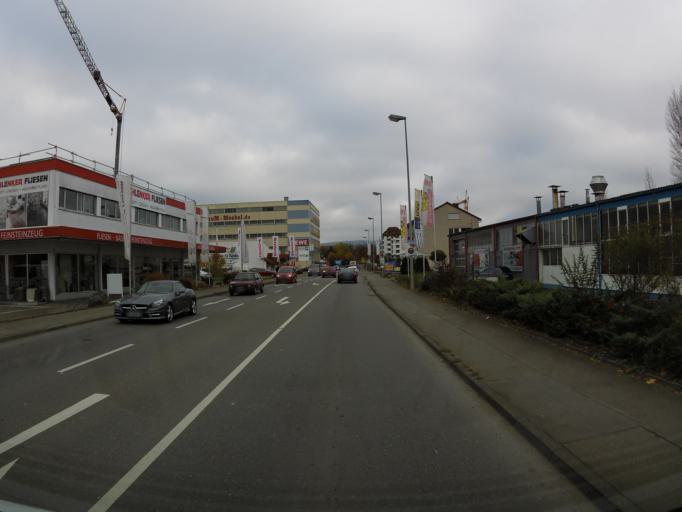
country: DE
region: Baden-Wuerttemberg
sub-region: Freiburg Region
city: Radolfzell am Bodensee
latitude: 47.7431
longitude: 8.9572
